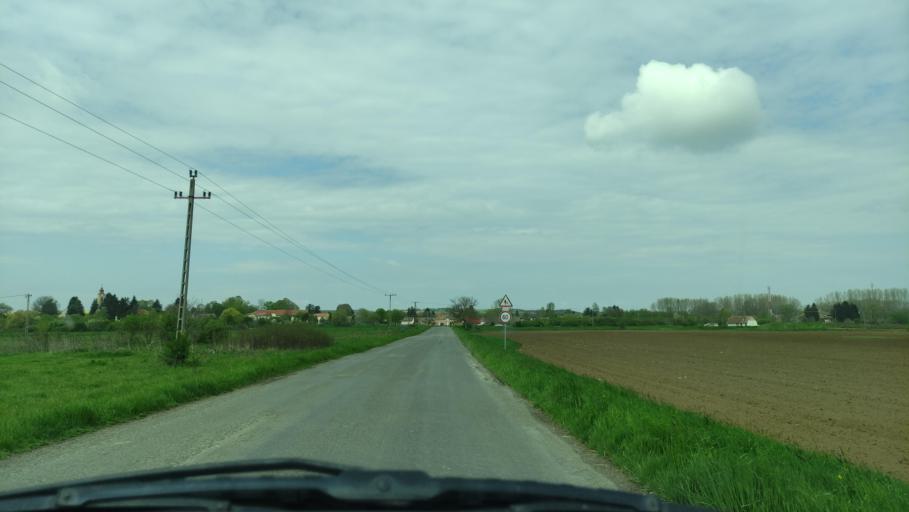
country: HU
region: Baranya
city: Sasd
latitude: 46.3059
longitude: 18.1436
